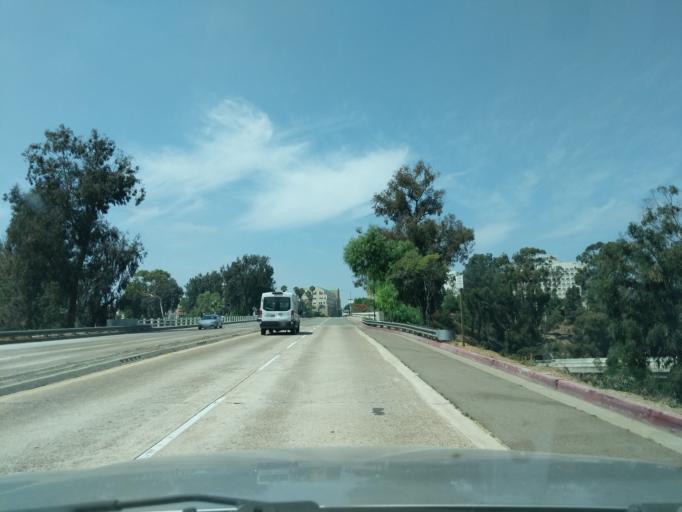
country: US
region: California
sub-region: San Diego County
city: San Diego
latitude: 32.7506
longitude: -117.1544
